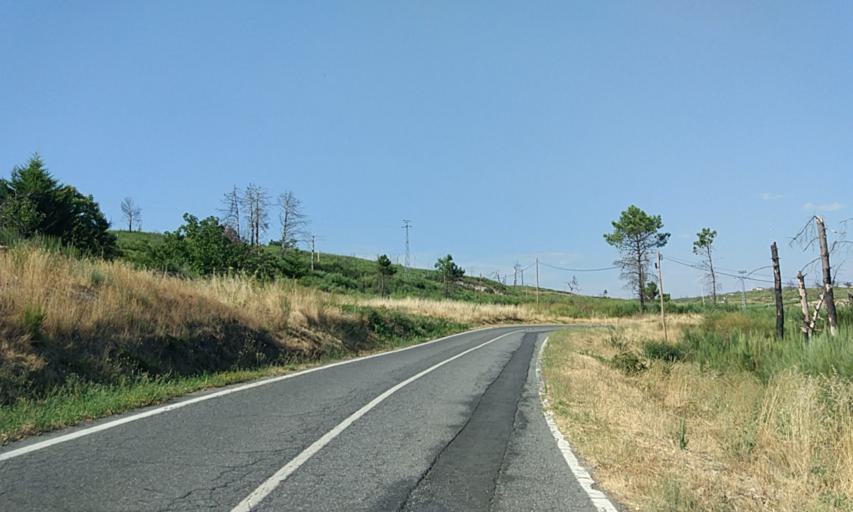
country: PT
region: Vila Real
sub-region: Murca
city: Murca
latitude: 41.3055
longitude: -7.4744
